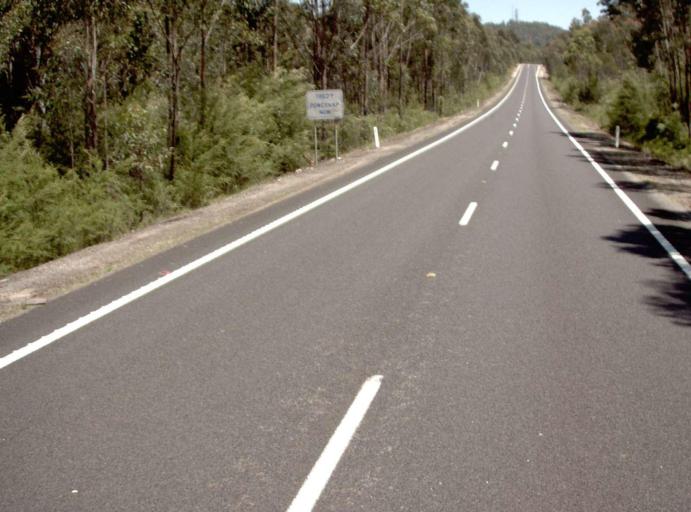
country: AU
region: Victoria
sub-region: East Gippsland
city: Lakes Entrance
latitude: -37.6948
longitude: 148.6129
